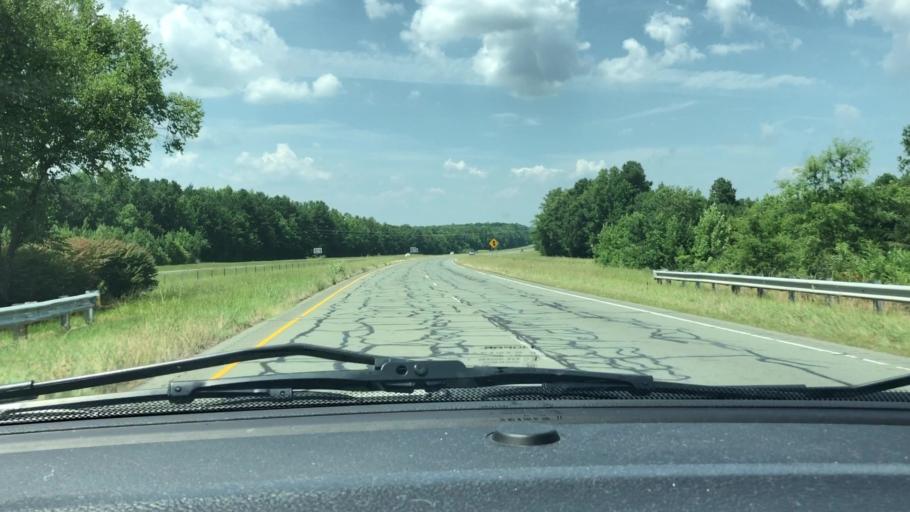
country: US
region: North Carolina
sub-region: Chatham County
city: Siler City
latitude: 35.6947
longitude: -79.4277
